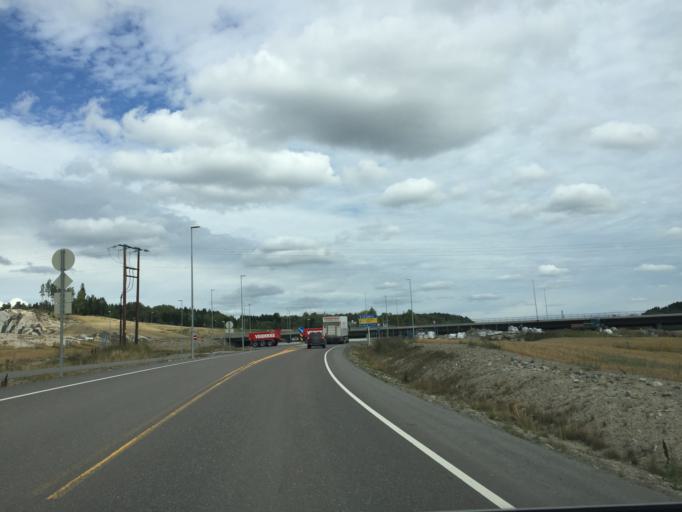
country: NO
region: Ostfold
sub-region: Hobol
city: Elvestad
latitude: 59.6265
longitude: 10.9544
